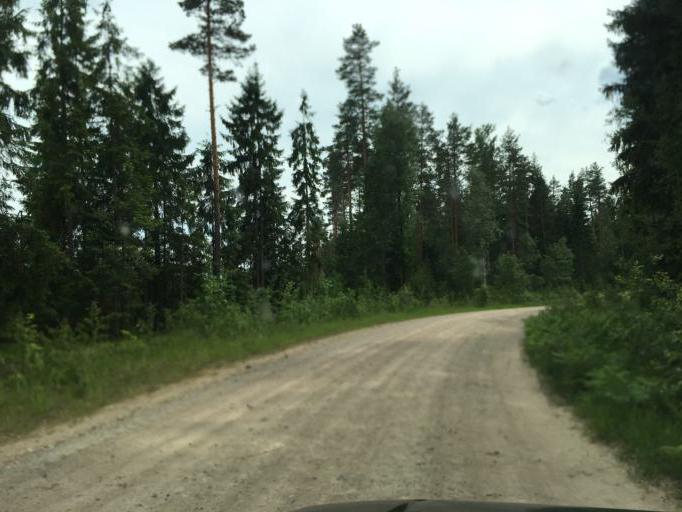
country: LV
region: Rugaju
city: Rugaji
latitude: 56.7674
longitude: 27.1066
